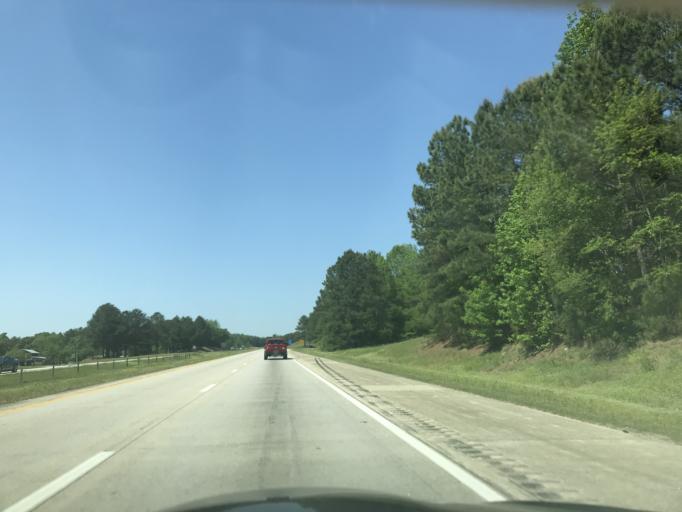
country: US
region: North Carolina
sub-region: Johnston County
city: Benson
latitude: 35.4328
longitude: -78.5325
